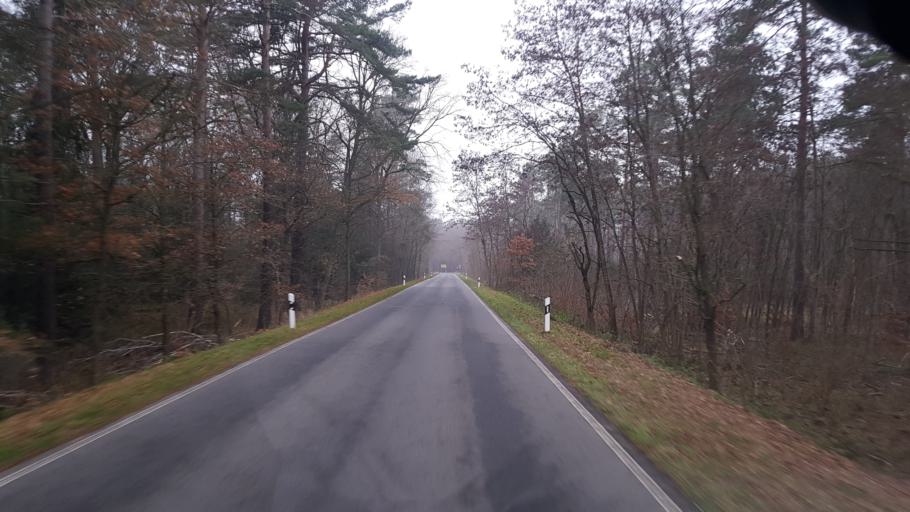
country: DE
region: Brandenburg
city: Bronkow
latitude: 51.6898
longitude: 13.9219
